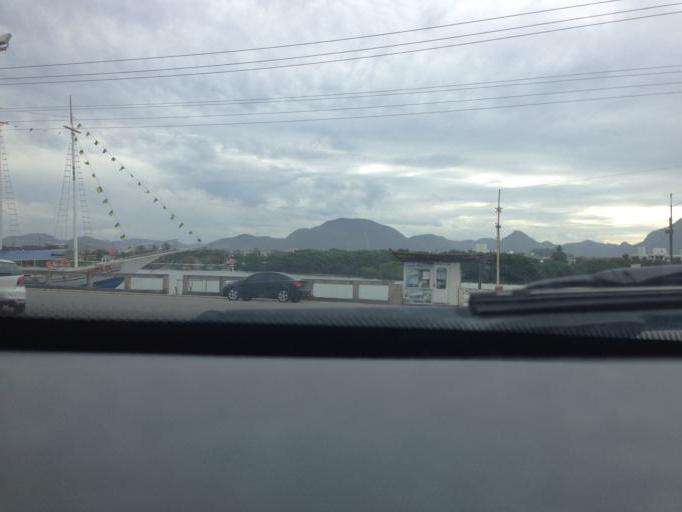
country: BR
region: Espirito Santo
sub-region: Guarapari
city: Guarapari
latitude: -20.6674
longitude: -40.4971
